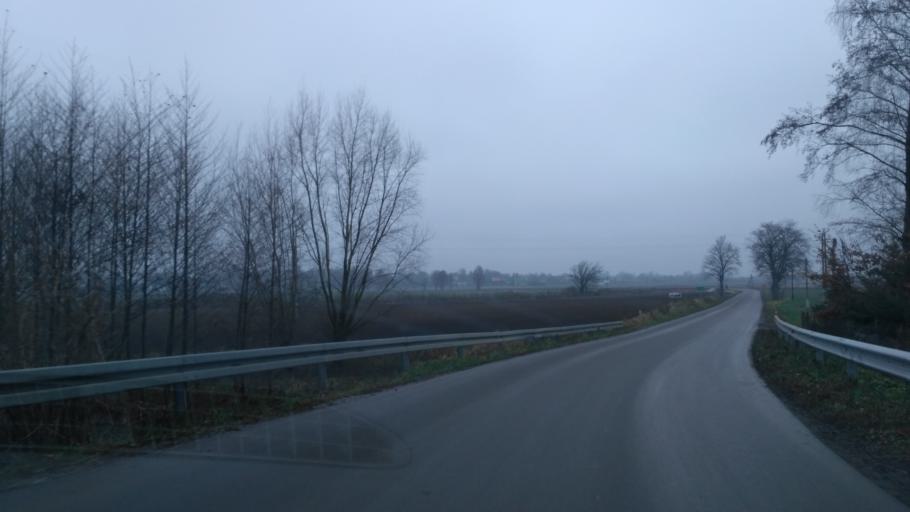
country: PL
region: Subcarpathian Voivodeship
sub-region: Powiat przeworski
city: Urzejowice
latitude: 50.0054
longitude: 22.4774
